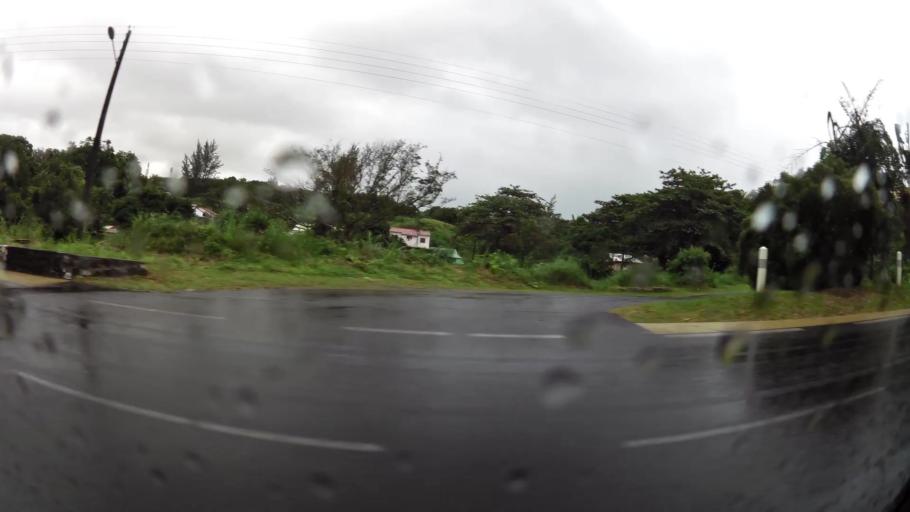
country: RE
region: Reunion
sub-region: Reunion
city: Saint-Benoit
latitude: -21.0220
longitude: 55.7025
